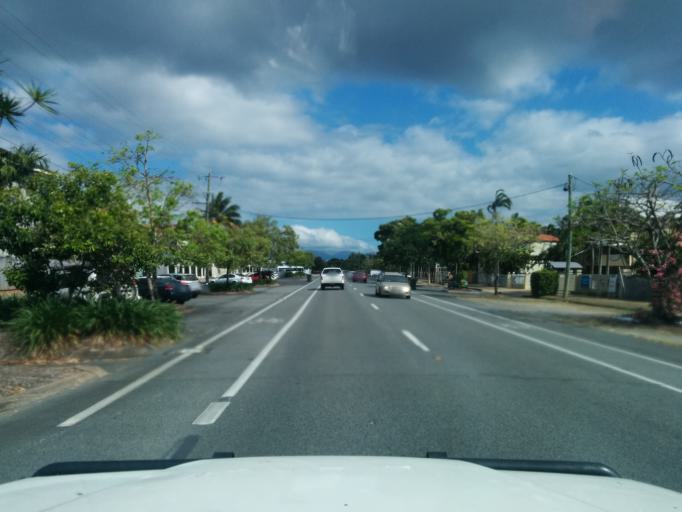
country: AU
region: Queensland
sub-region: Cairns
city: Cairns
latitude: -16.9108
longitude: 145.7615
